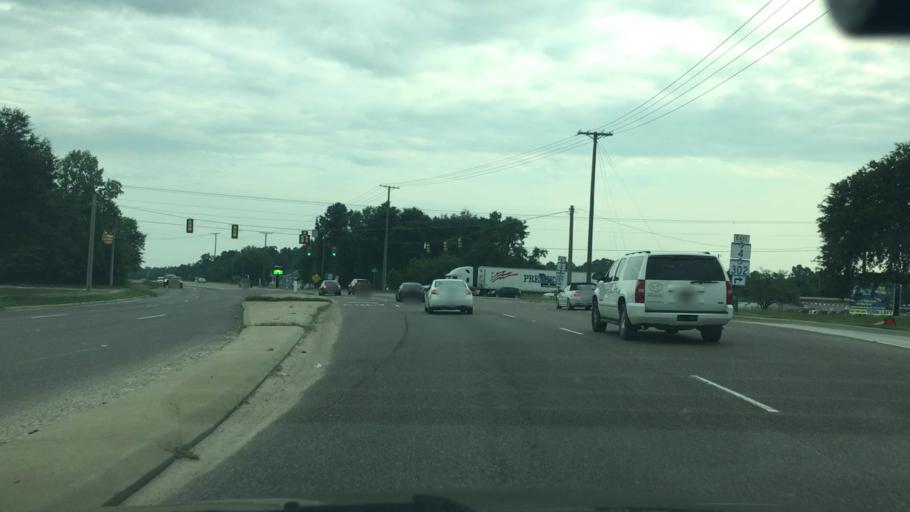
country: US
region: South Carolina
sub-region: Aiken County
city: Aiken
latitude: 33.5457
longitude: -81.6779
